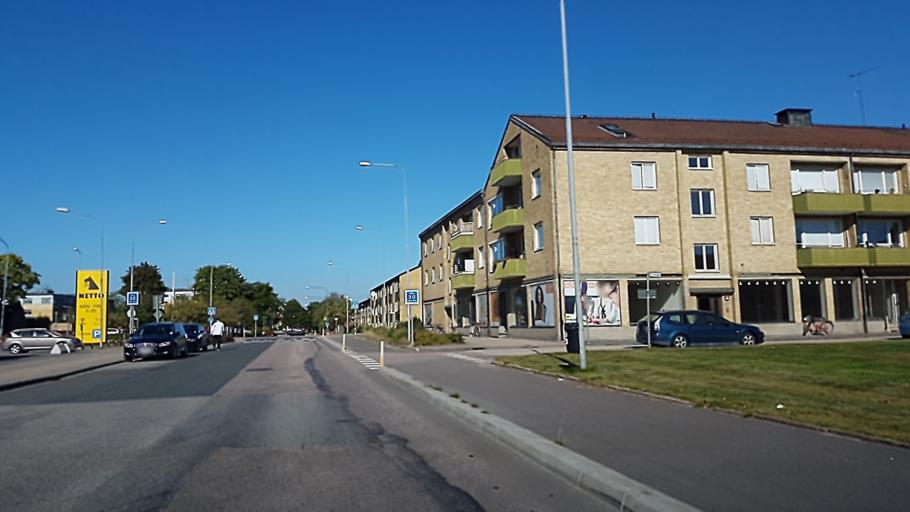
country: SE
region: Kronoberg
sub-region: Ljungby Kommun
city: Ljungby
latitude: 56.8292
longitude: 13.9530
